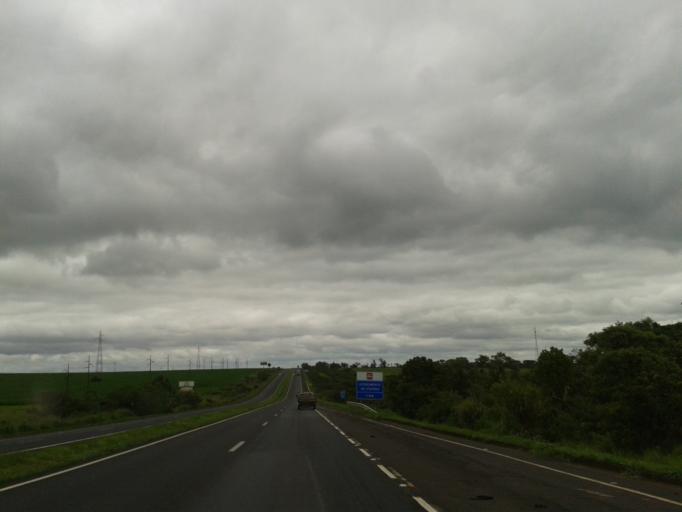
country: BR
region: Minas Gerais
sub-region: Uberlandia
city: Uberlandia
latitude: -19.0339
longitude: -48.2012
